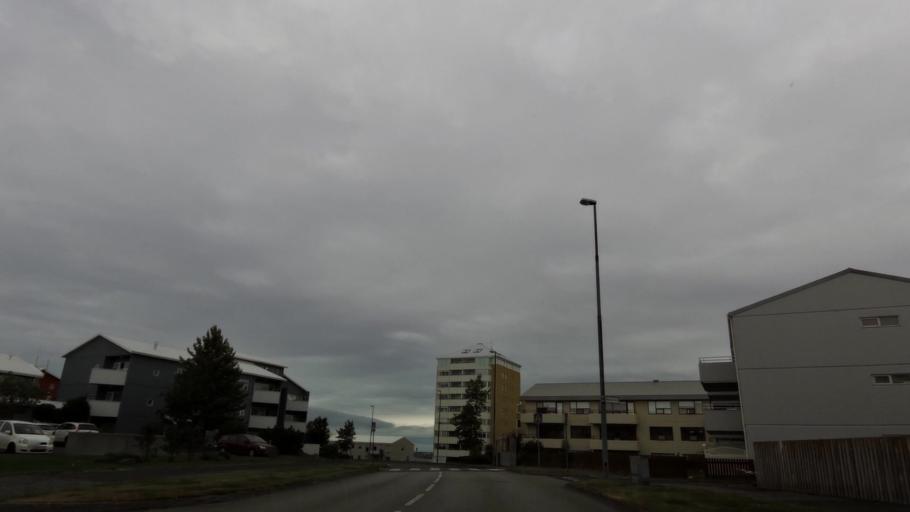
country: IS
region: Capital Region
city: Hafnarfjoerdur
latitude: 64.0566
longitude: -21.9826
